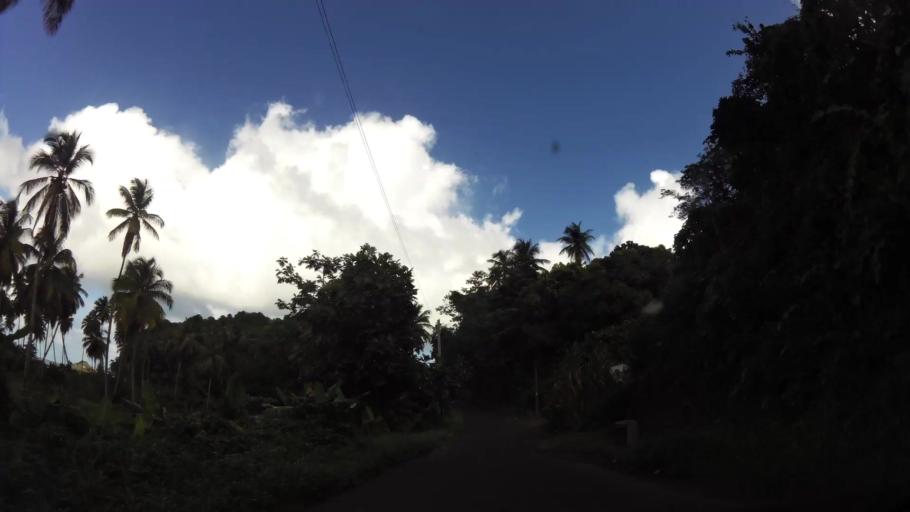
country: DM
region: Saint Andrew
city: Calibishie
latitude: 15.5917
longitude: -61.3813
